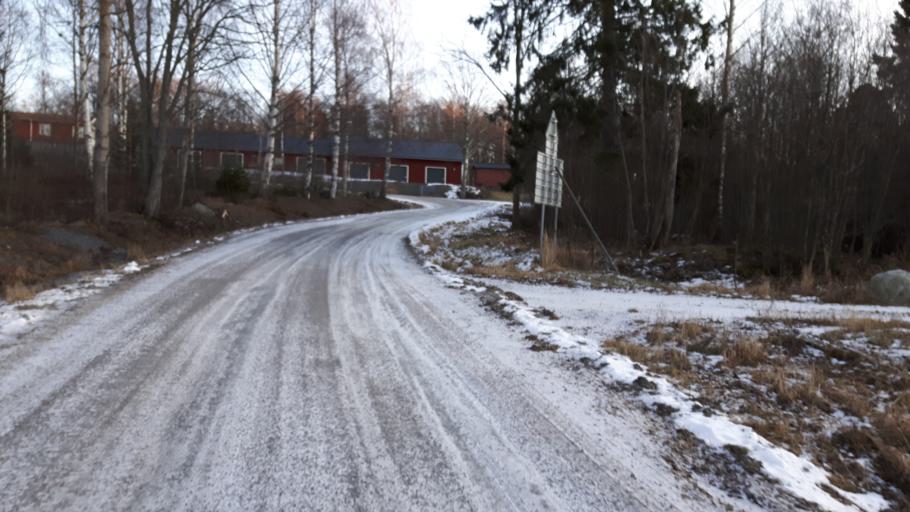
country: SE
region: Vaesternorrland
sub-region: Haernoesands Kommun
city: Haernoesand
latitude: 62.6198
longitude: 17.9375
